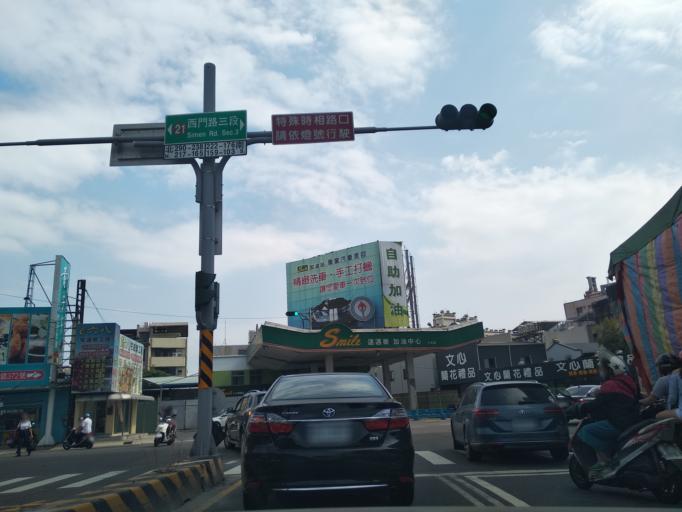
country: TW
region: Taiwan
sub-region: Tainan
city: Tainan
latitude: 23.0040
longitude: 120.2042
